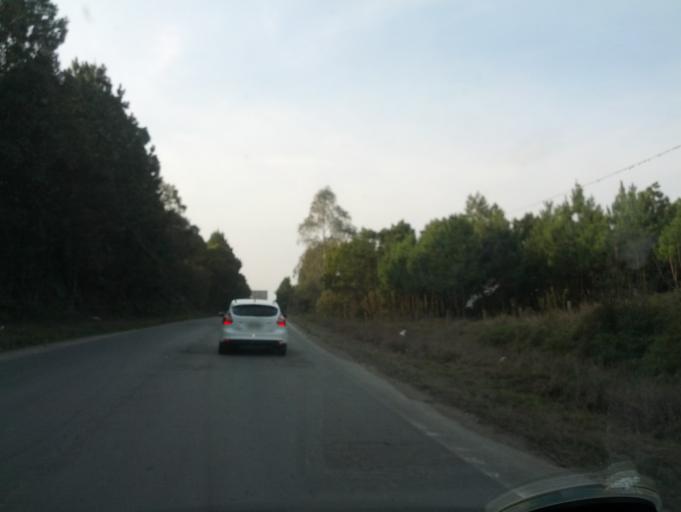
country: BR
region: Santa Catarina
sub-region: Otacilio Costa
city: Otacilio Costa
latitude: -27.5483
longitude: -50.1474
